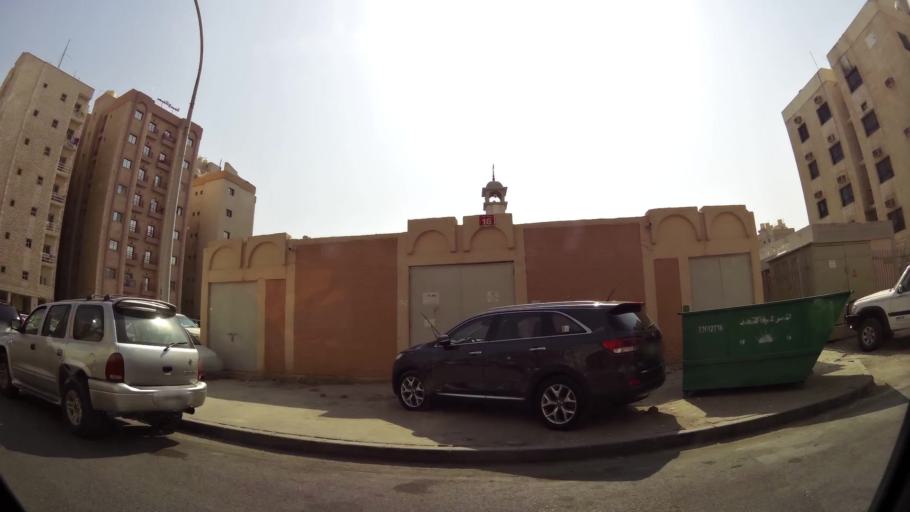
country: KW
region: Muhafazat Hawalli
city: Hawalli
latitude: 29.3370
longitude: 48.0106
